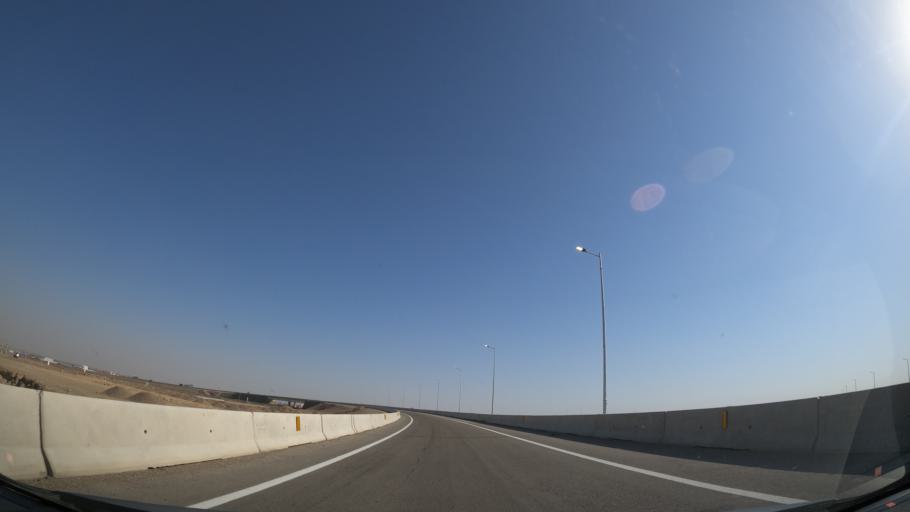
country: IR
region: Tehran
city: Eqbaliyeh
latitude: 35.1345
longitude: 51.5090
